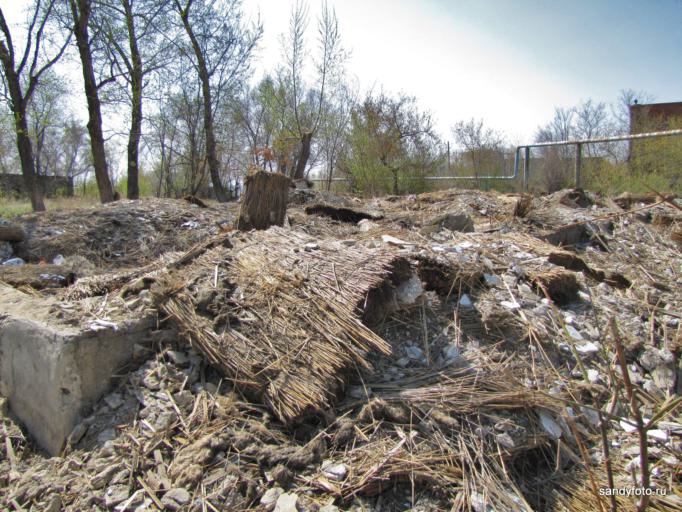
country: RU
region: Chelyabinsk
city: Troitsk
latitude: 54.1009
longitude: 61.5540
